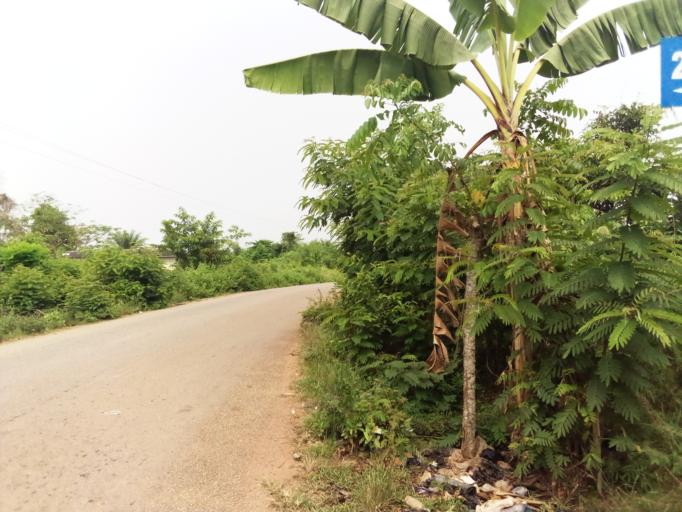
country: CI
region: Sud-Comoe
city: Ayame
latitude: 5.8316
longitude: -2.8204
